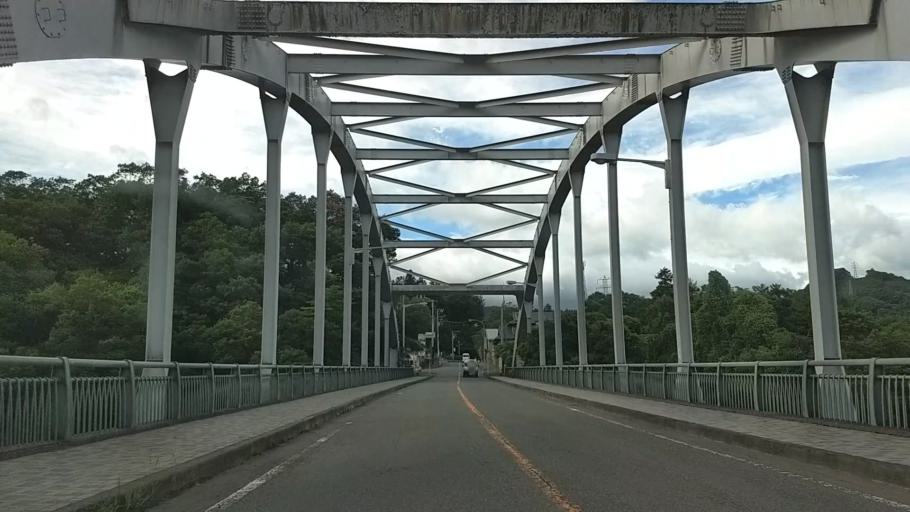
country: JP
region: Yamanashi
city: Uenohara
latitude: 35.5973
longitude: 139.1522
